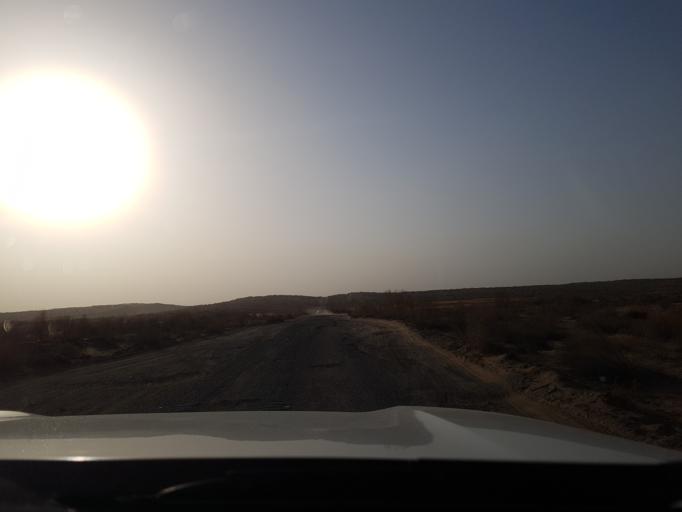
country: UZ
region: Xorazm
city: Hazorasp
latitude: 41.1719
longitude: 60.8122
